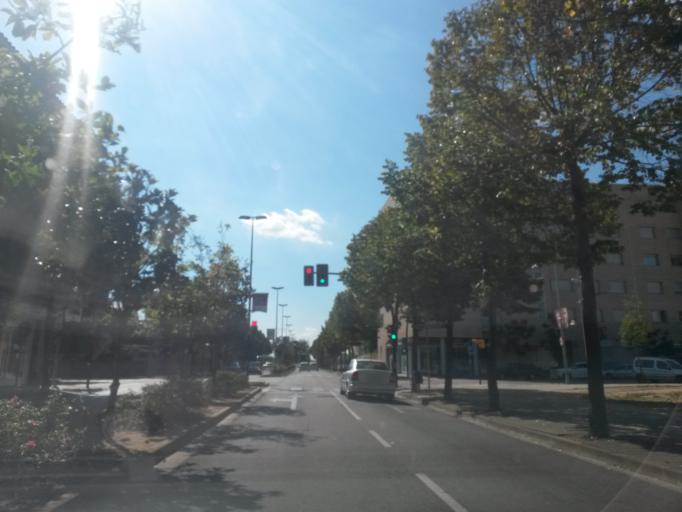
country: ES
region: Catalonia
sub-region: Provincia de Girona
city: Salt
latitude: 41.9689
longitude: 2.7871
